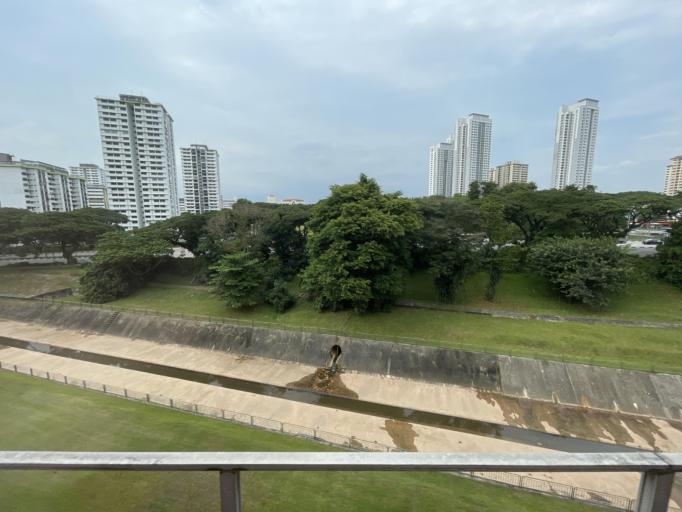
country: SG
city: Singapore
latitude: 1.3074
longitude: 103.7900
